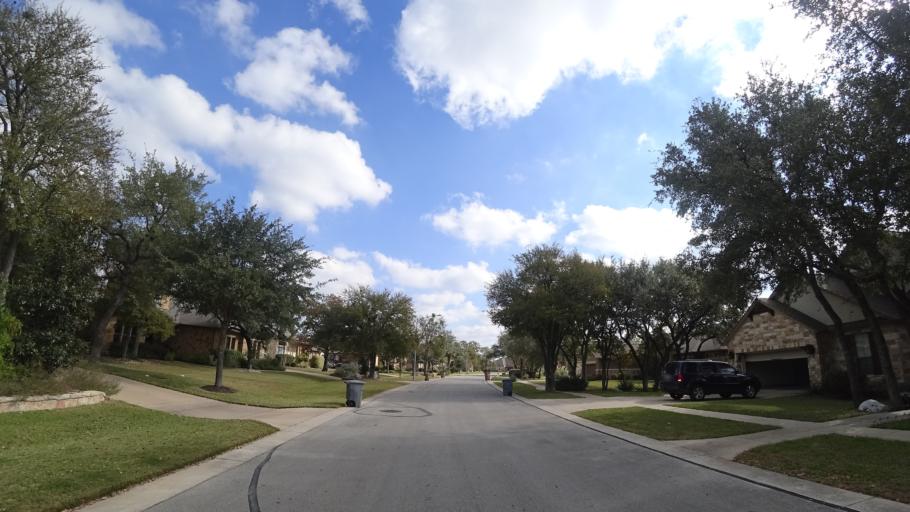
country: US
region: Texas
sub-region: Travis County
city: Shady Hollow
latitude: 30.1746
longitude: -97.8521
